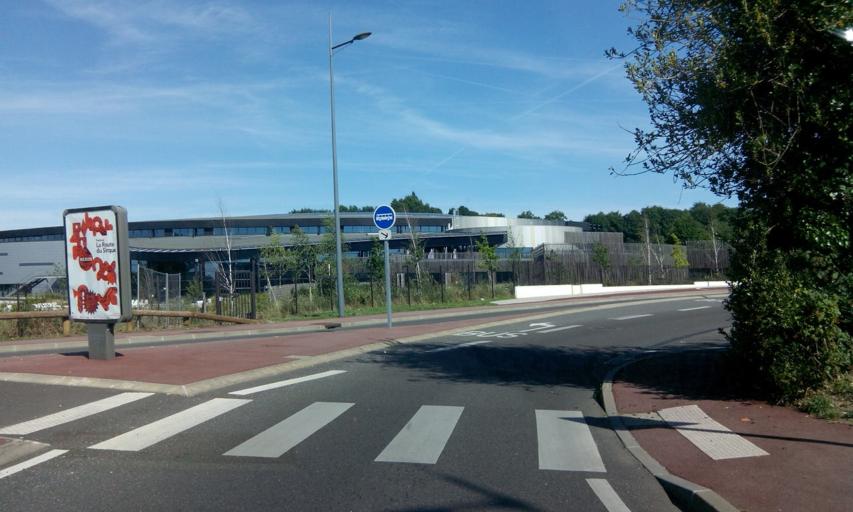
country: FR
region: Limousin
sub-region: Departement de la Haute-Vienne
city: Limoges
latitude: 45.8551
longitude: 1.2837
